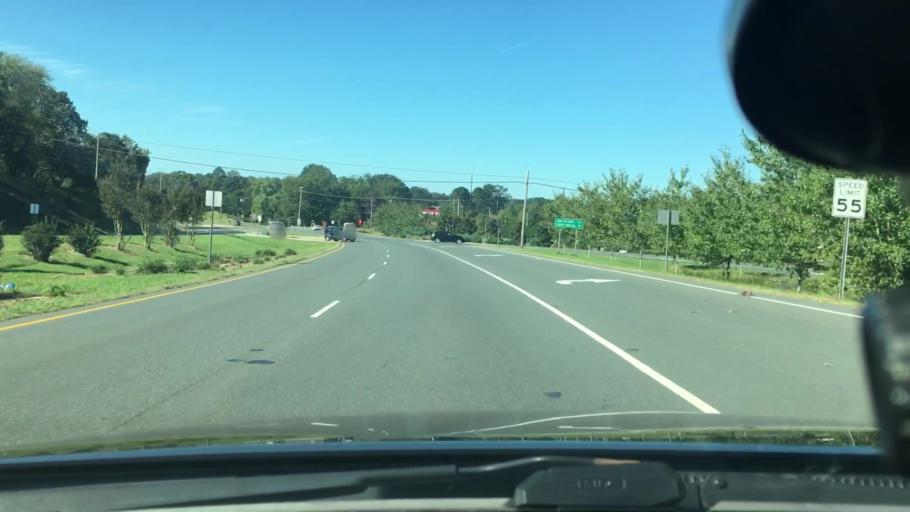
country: US
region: North Carolina
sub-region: Stanly County
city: Albemarle
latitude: 35.3340
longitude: -80.2310
